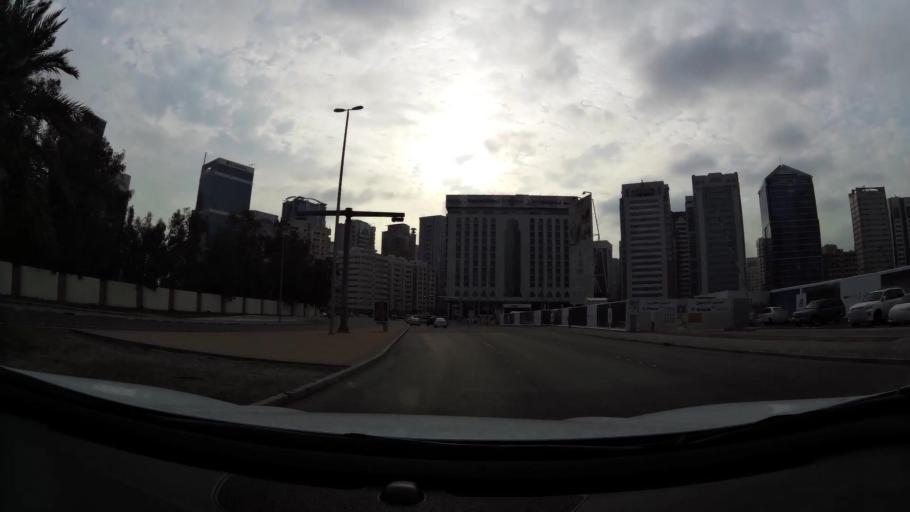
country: AE
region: Abu Dhabi
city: Abu Dhabi
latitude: 24.5036
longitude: 54.3721
